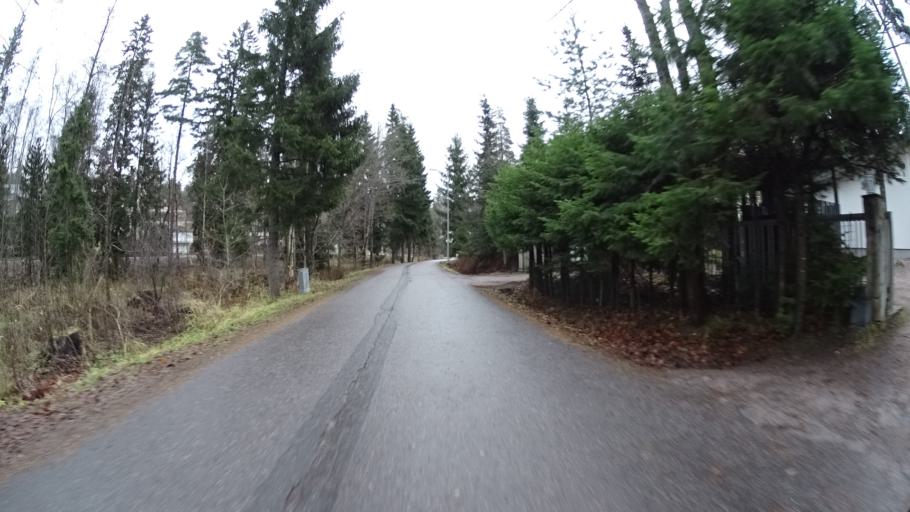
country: FI
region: Uusimaa
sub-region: Helsinki
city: Kauniainen
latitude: 60.2206
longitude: 24.7286
